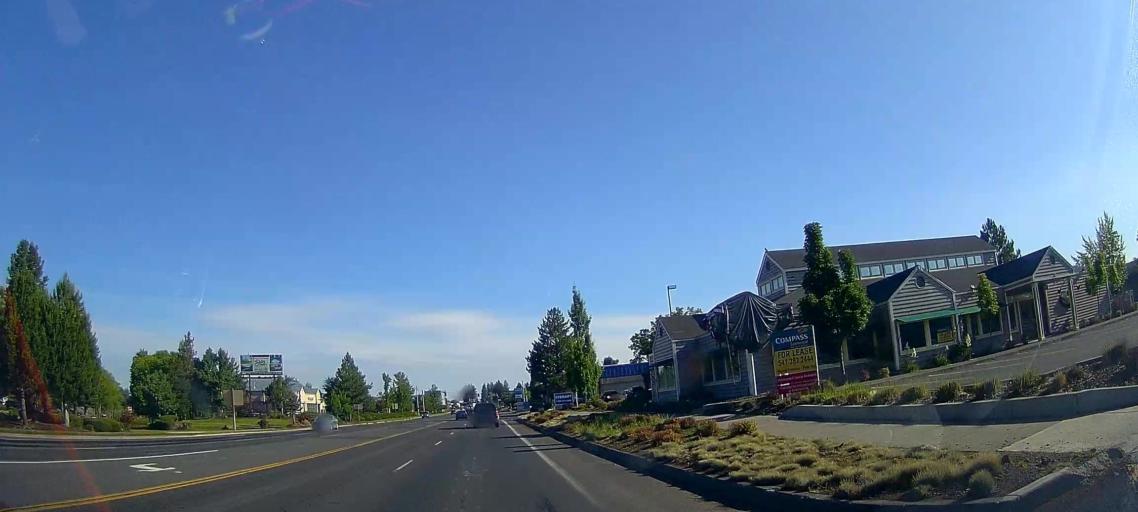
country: US
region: Oregon
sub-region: Deschutes County
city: Bend
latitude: 44.0819
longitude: -121.3052
